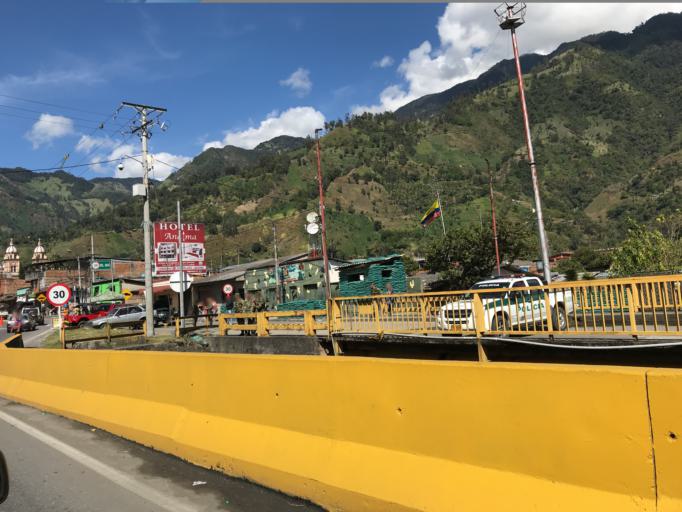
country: CO
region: Tolima
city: Cajamarca
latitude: 4.4415
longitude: -75.4244
